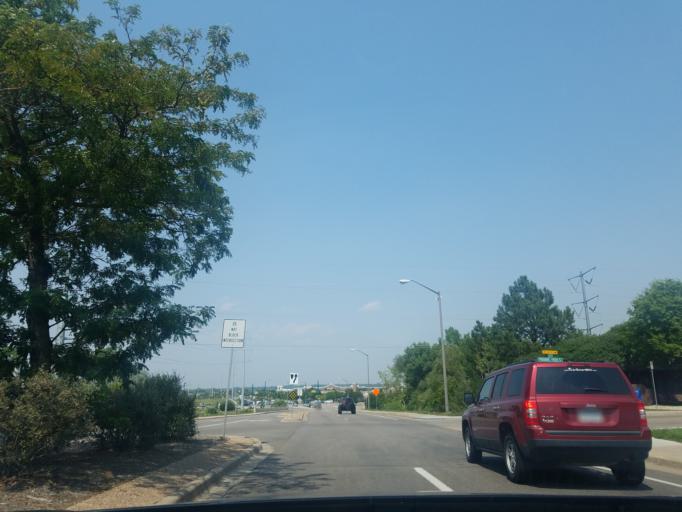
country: US
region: Colorado
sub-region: Larimer County
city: Fort Collins
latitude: 40.5788
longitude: -105.0576
